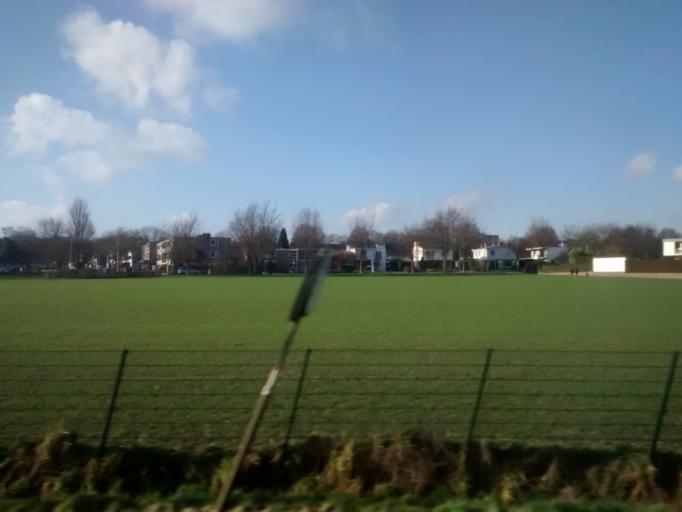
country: NL
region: Limburg
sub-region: Gemeente Schinnen
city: Puth
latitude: 50.9547
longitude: 5.8361
